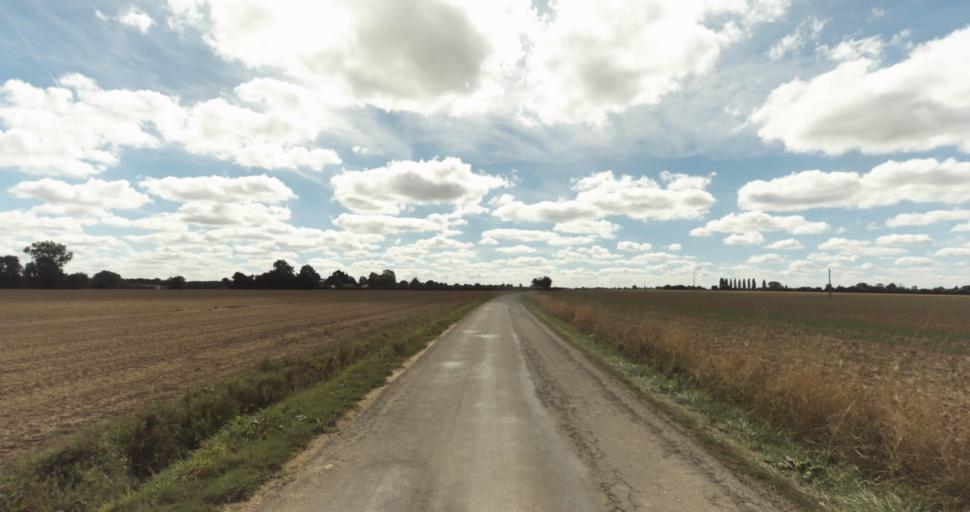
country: FR
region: Lower Normandy
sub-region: Departement du Calvados
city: Orbec
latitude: 48.9196
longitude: 0.3755
